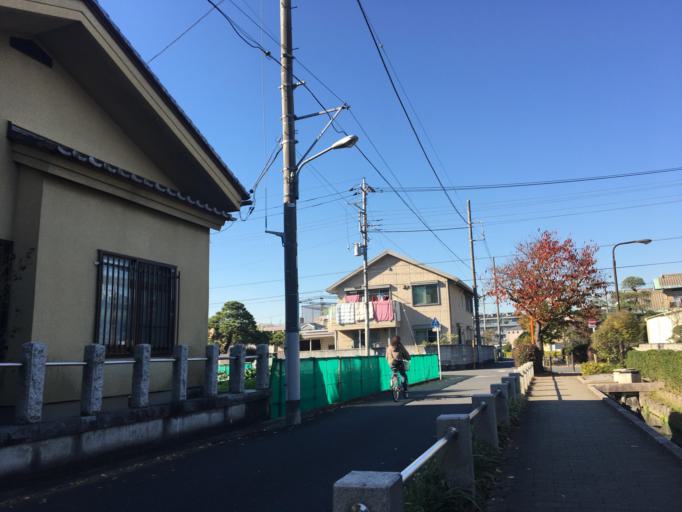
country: JP
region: Tokyo
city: Urayasu
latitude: 35.6938
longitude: 139.9042
